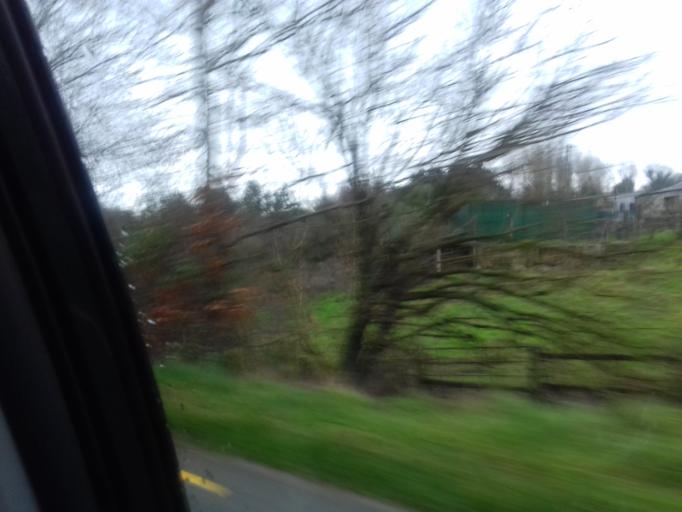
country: IE
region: Leinster
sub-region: Kilkenny
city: Graiguenamanagh
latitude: 52.6152
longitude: -6.9895
